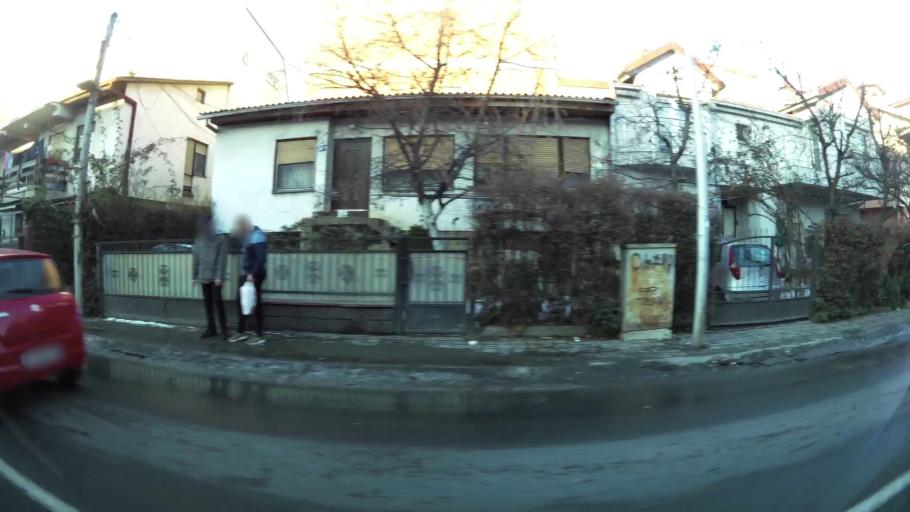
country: MK
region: Karpos
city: Skopje
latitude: 41.9938
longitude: 21.4022
